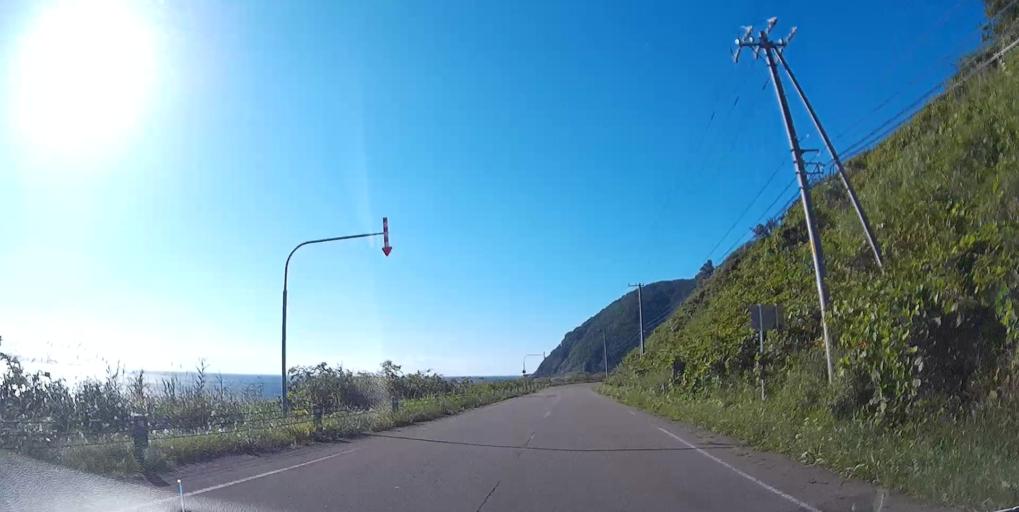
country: JP
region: Hokkaido
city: Kamiiso
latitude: 42.2456
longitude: 139.7877
